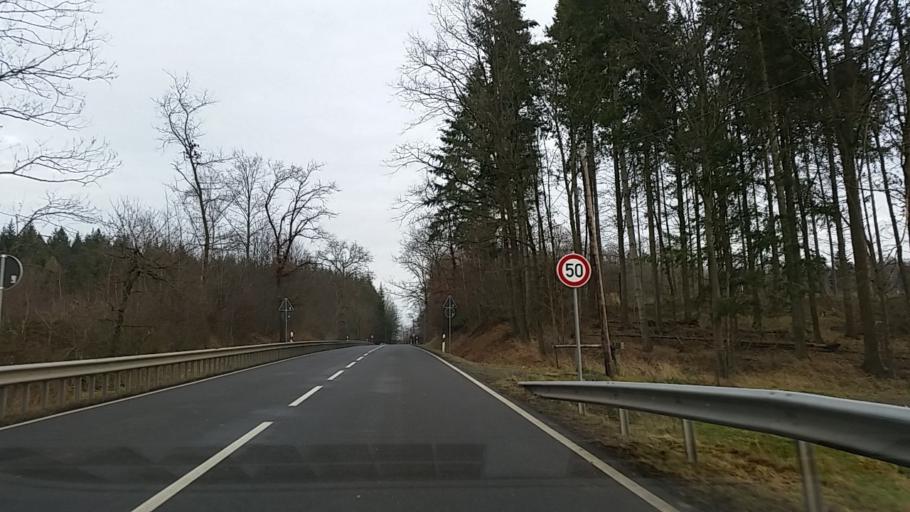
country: DE
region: Lower Saxony
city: Alt Wallmoden
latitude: 52.0118
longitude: 10.3059
